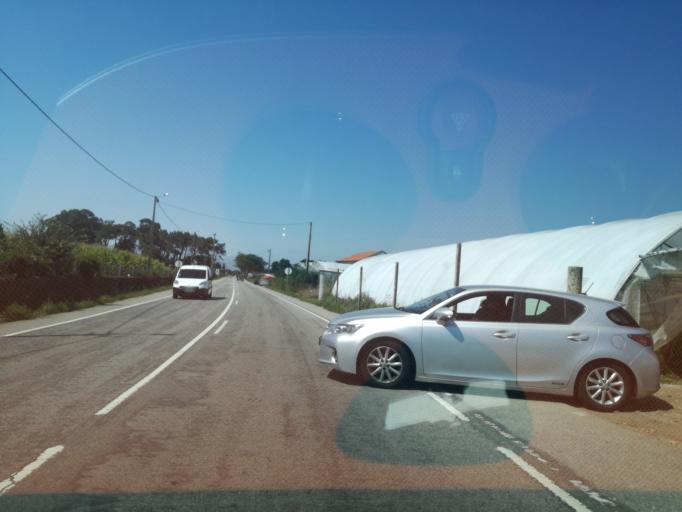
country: PT
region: Braga
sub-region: Esposende
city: Apulia
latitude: 41.4949
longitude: -8.7560
